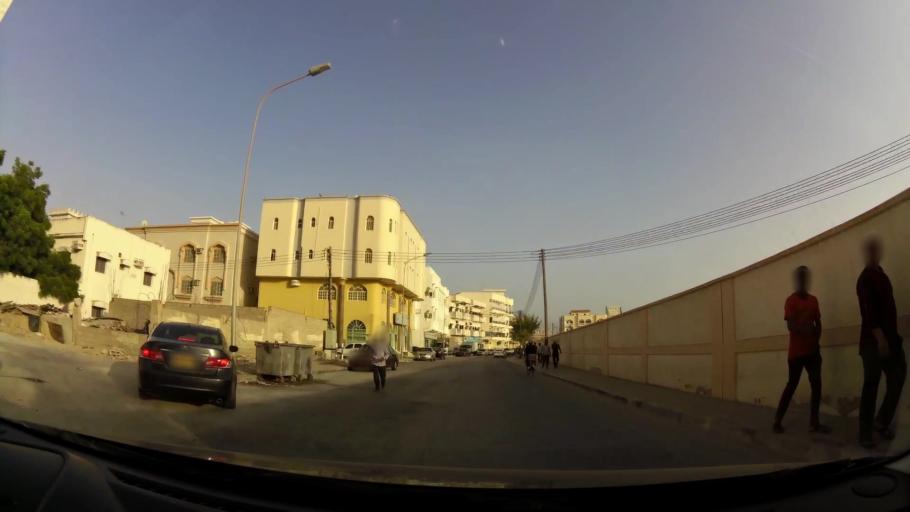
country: OM
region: Zufar
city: Salalah
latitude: 17.0159
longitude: 54.0969
